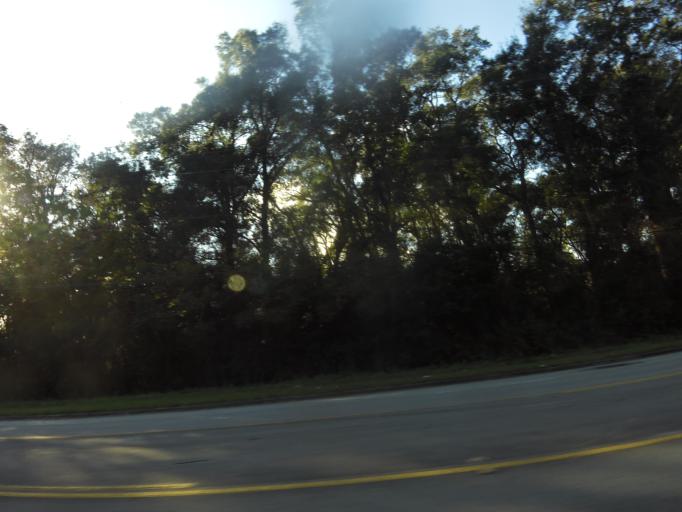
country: US
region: Florida
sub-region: Duval County
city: Jacksonville
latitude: 30.3281
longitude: -81.5601
